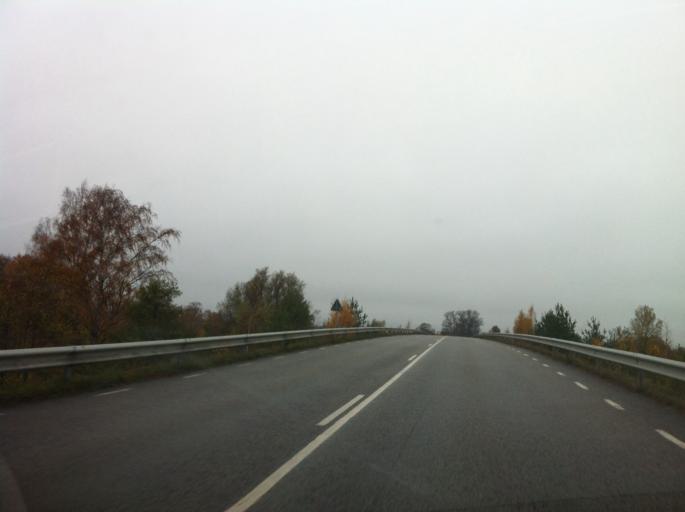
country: SE
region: Skane
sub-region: Kavlinge Kommun
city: Loddekopinge
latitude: 55.8187
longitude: 13.0386
